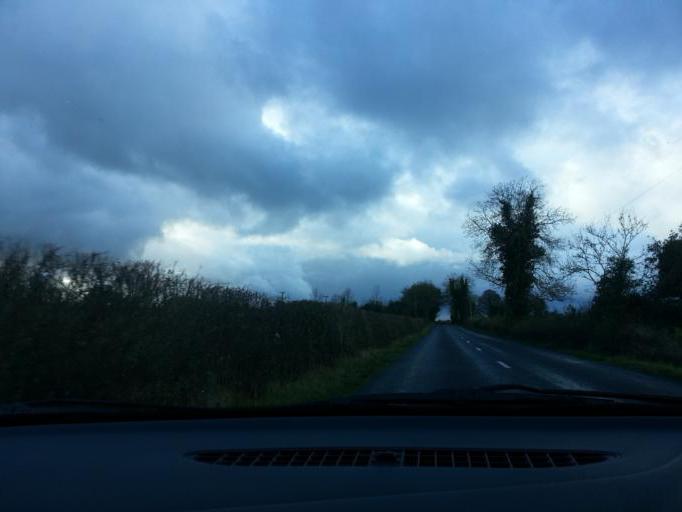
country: IE
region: Ulster
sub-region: County Monaghan
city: Clones
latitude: 54.2272
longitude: -7.3029
